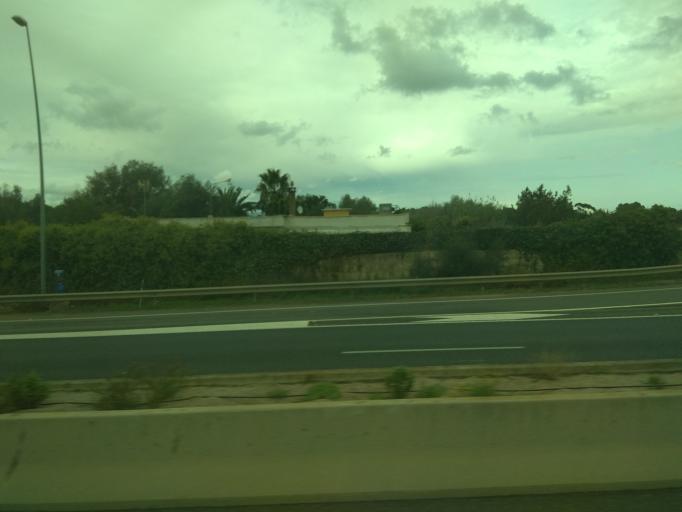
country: ES
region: Balearic Islands
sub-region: Illes Balears
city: Algaida
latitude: 39.5696
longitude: 2.8494
